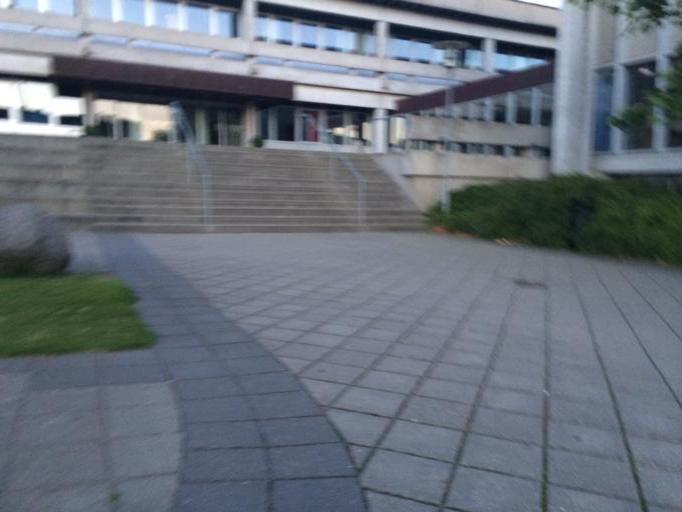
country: DK
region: South Denmark
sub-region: Vejle Kommune
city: Vejle
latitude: 55.7105
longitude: 9.5542
